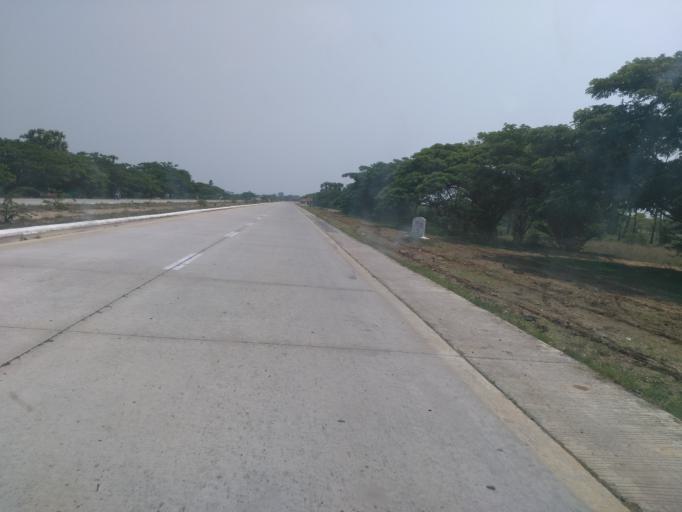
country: MM
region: Sagain
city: Sagaing
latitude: 21.8133
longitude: 95.9793
